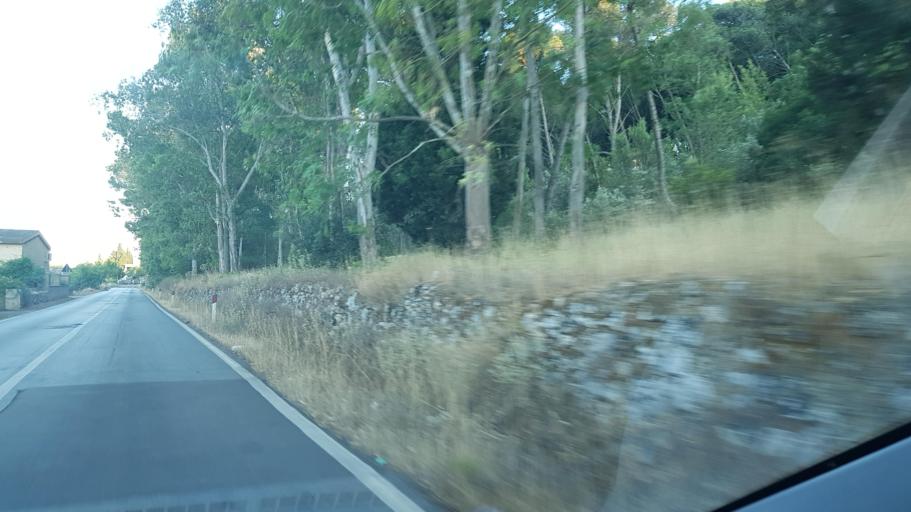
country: IT
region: Apulia
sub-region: Provincia di Lecce
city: Specchia
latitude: 39.9503
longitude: 18.2911
